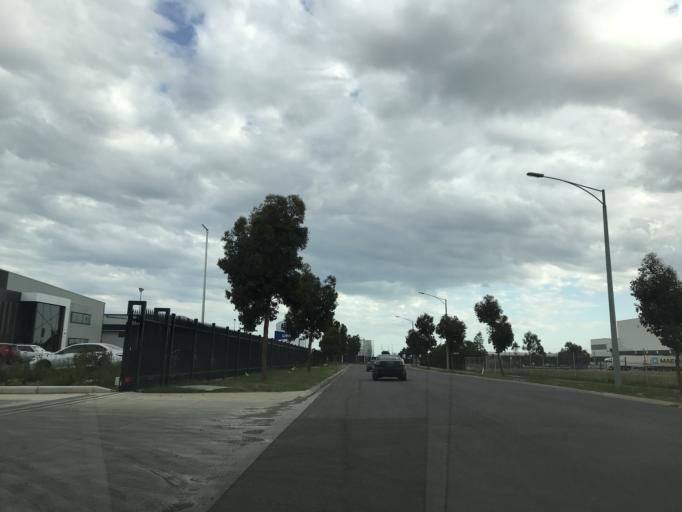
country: AU
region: Victoria
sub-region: Wyndham
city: Truganina
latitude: -37.8202
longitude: 144.7384
